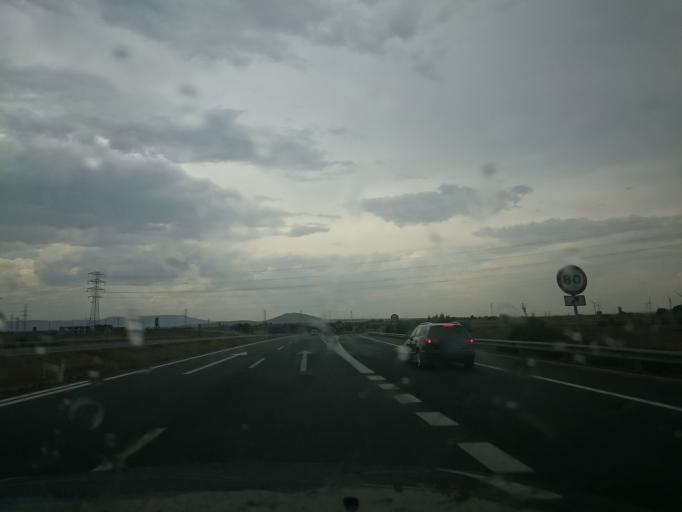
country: ES
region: Aragon
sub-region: Provincia de Zaragoza
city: Gallur
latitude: 41.8498
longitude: -1.3719
